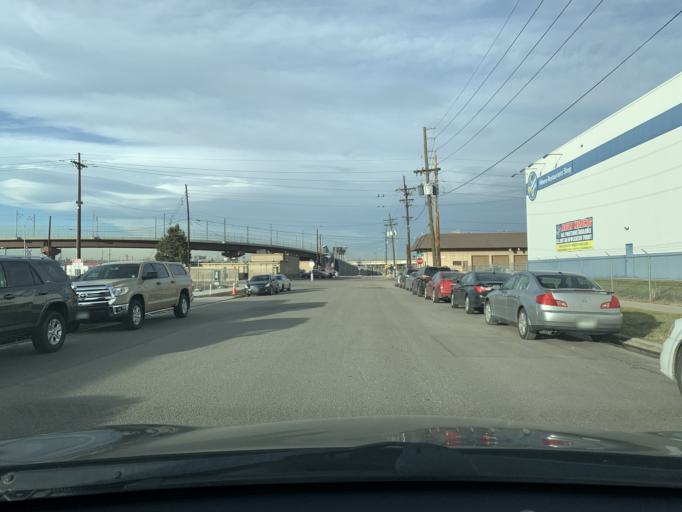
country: US
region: Colorado
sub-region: Denver County
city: Denver
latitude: 39.7363
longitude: -105.0102
